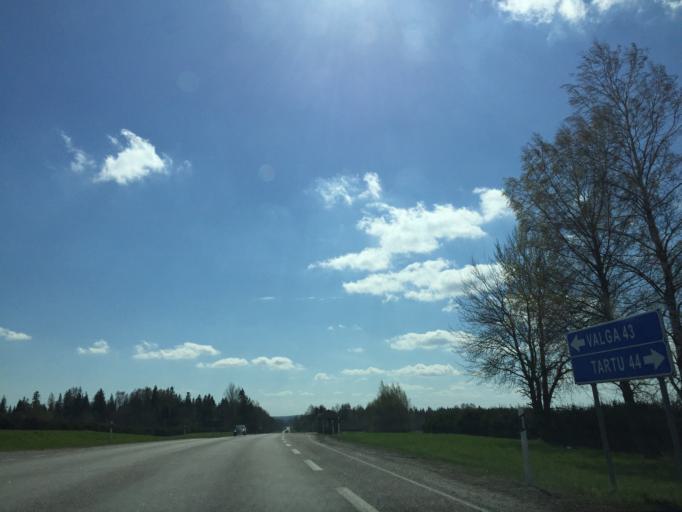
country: EE
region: Tartu
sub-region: Elva linn
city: Elva
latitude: 58.1102
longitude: 26.2398
